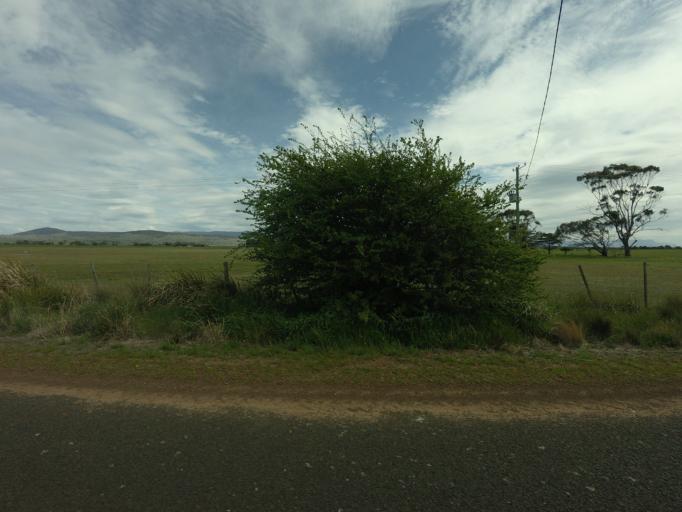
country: AU
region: Tasmania
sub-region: Northern Midlands
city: Evandale
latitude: -41.8531
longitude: 147.3412
